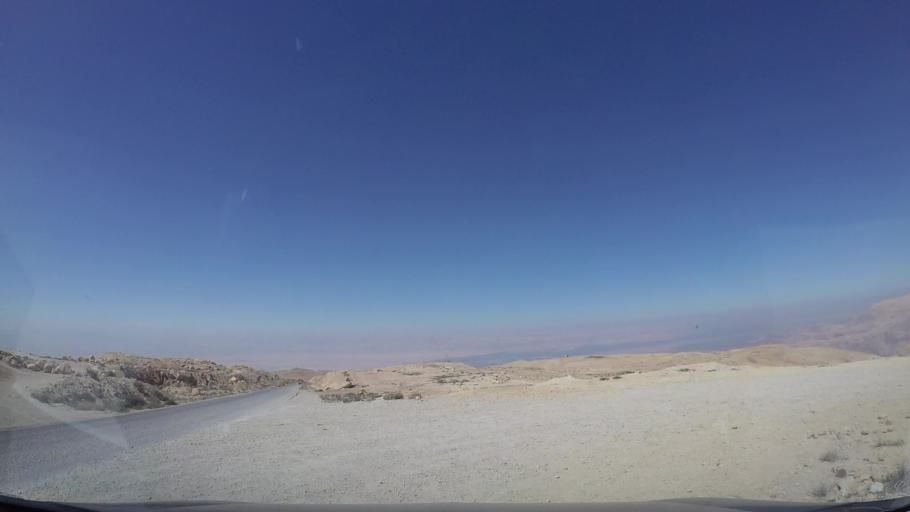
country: JO
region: Tafielah
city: At Tafilah
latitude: 30.8603
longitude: 35.5384
